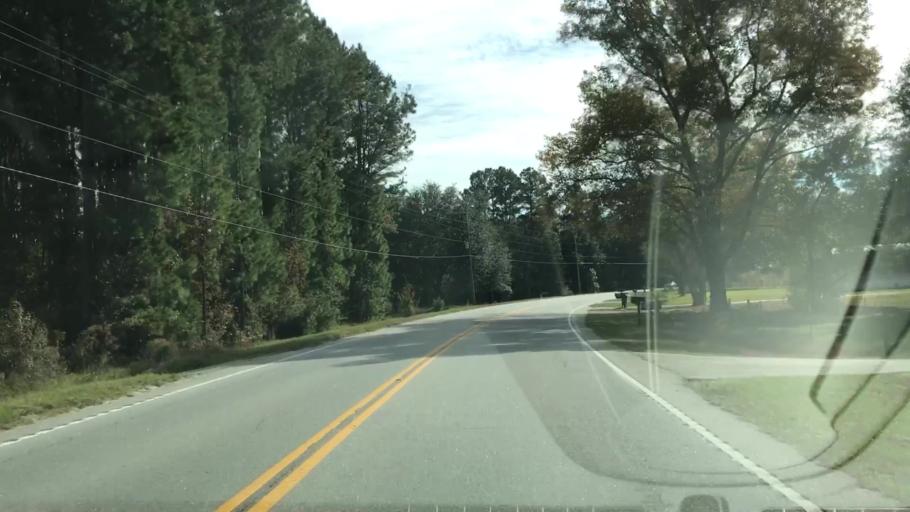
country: US
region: South Carolina
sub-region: Colleton County
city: Walterboro
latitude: 32.8586
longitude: -80.6012
